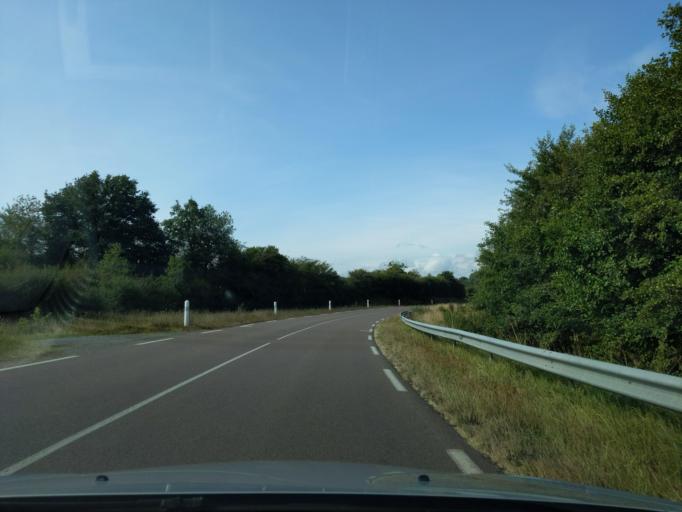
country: FR
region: Bourgogne
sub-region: Departement de Saone-et-Loire
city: Etang-sur-Arroux
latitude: 46.8994
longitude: 4.1614
